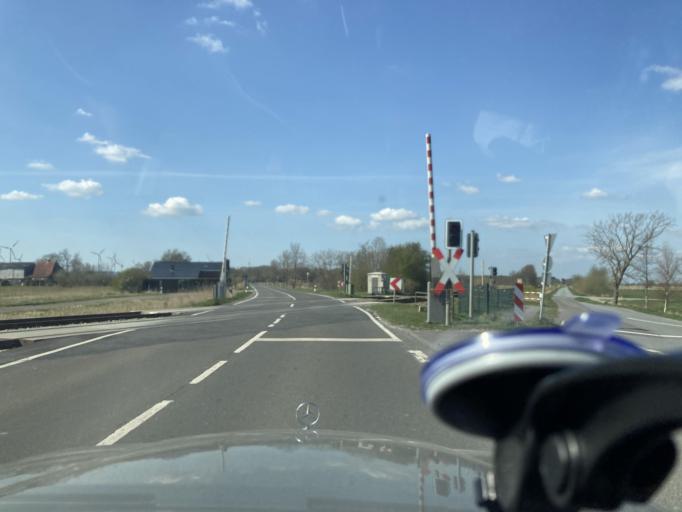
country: DE
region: Schleswig-Holstein
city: Stelle-Wittenwurth
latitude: 54.2587
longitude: 9.0581
